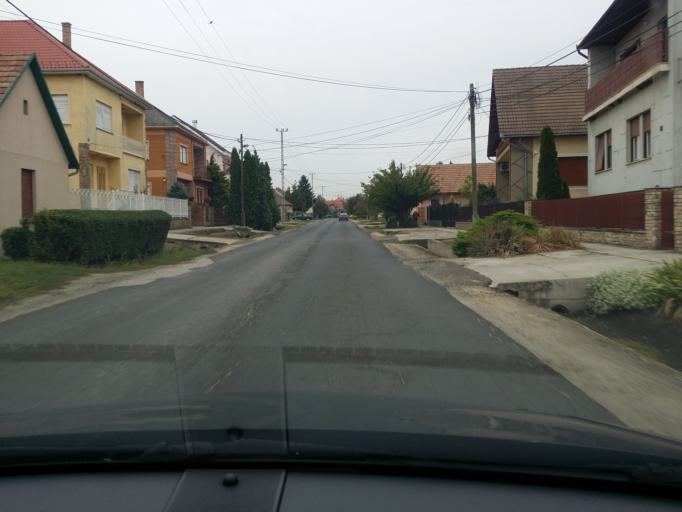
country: HU
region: Pest
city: Alsonemedi
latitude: 47.3196
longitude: 19.1531
